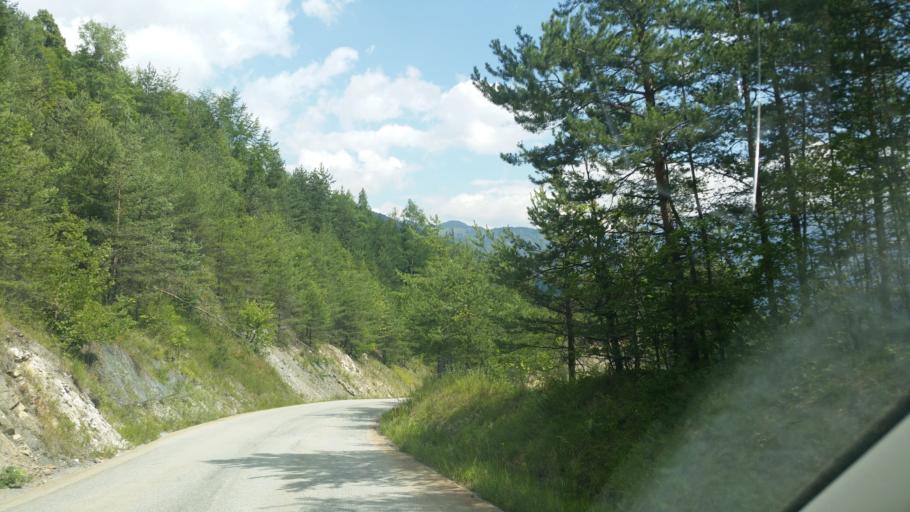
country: FR
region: Rhone-Alpes
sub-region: Departement de la Savoie
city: Saint-Jean-de-Maurienne
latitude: 45.2335
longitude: 6.3116
